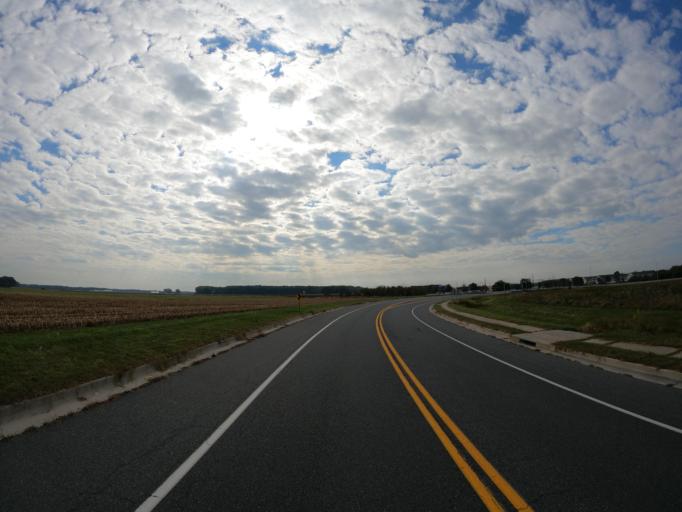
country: US
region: Delaware
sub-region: Sussex County
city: Bridgeville
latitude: 38.7225
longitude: -75.5854
